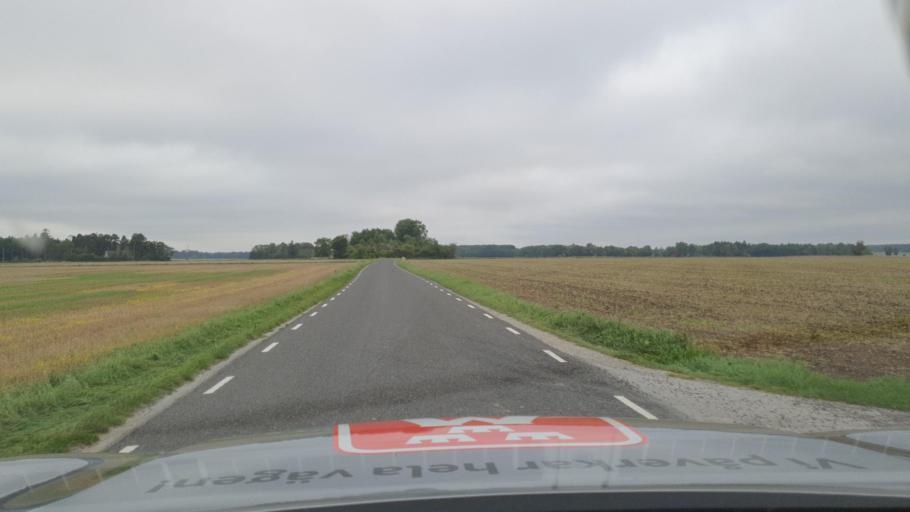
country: SE
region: Gotland
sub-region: Gotland
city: Visby
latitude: 57.6204
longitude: 18.4689
